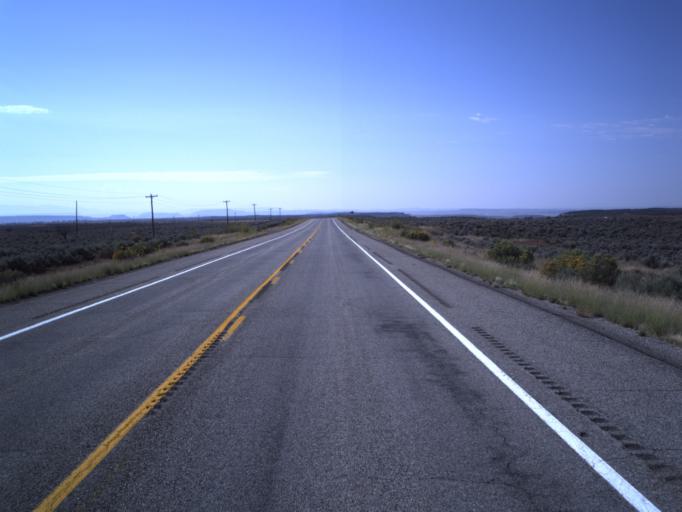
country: US
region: Utah
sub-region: San Juan County
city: Blanding
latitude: 37.5207
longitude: -109.4941
